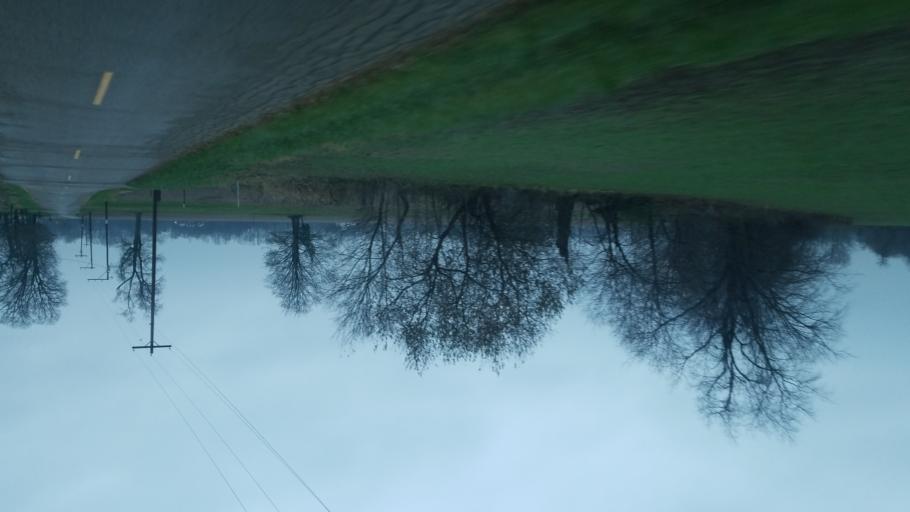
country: US
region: Ohio
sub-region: Knox County
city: Fredericktown
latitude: 40.4349
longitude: -82.5372
